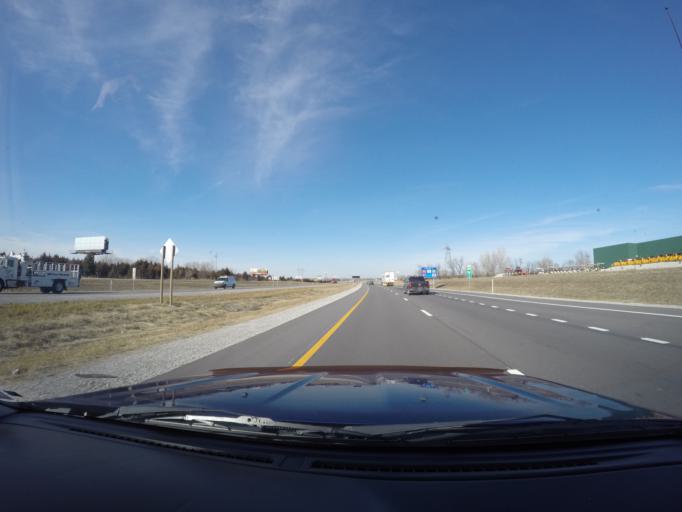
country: US
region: Kansas
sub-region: Sedgwick County
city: Park City
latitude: 37.7870
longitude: -97.3260
